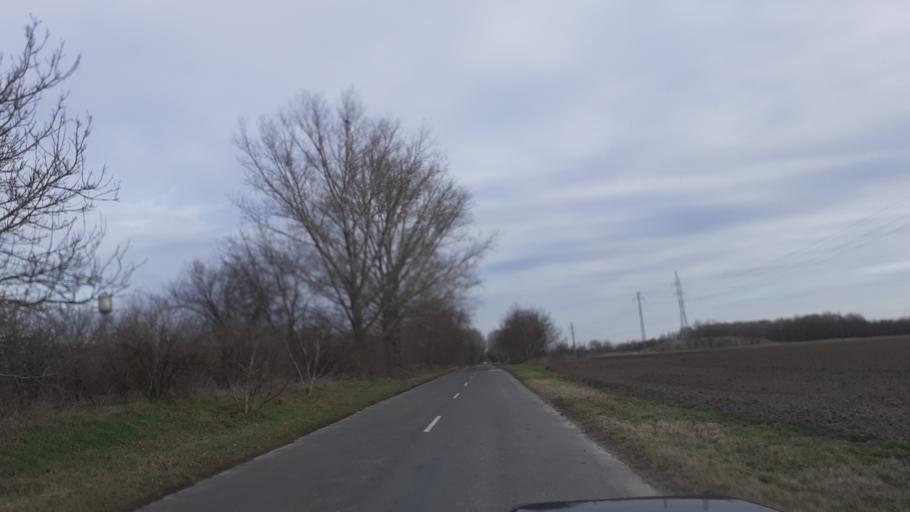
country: HU
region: Fejer
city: Szabadbattyan
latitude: 47.1250
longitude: 18.3839
